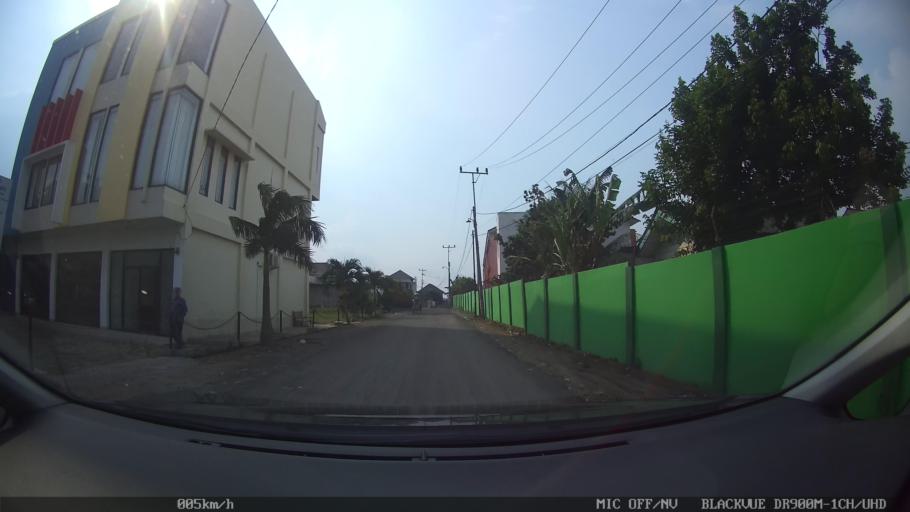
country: ID
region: Lampung
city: Kedaton
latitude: -5.3658
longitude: 105.2189
